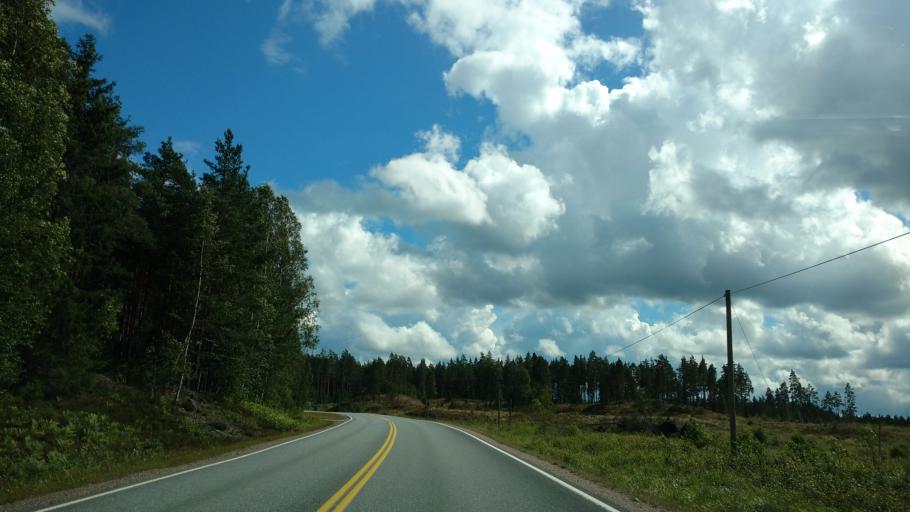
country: FI
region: Varsinais-Suomi
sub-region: Salo
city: Kisko
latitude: 60.2357
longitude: 23.5859
